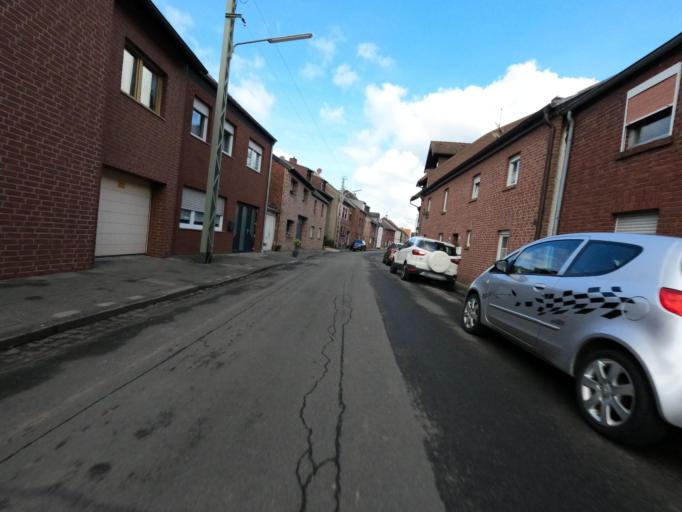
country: DE
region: North Rhine-Westphalia
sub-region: Regierungsbezirk Koln
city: Linnich
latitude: 51.0139
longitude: 6.2705
